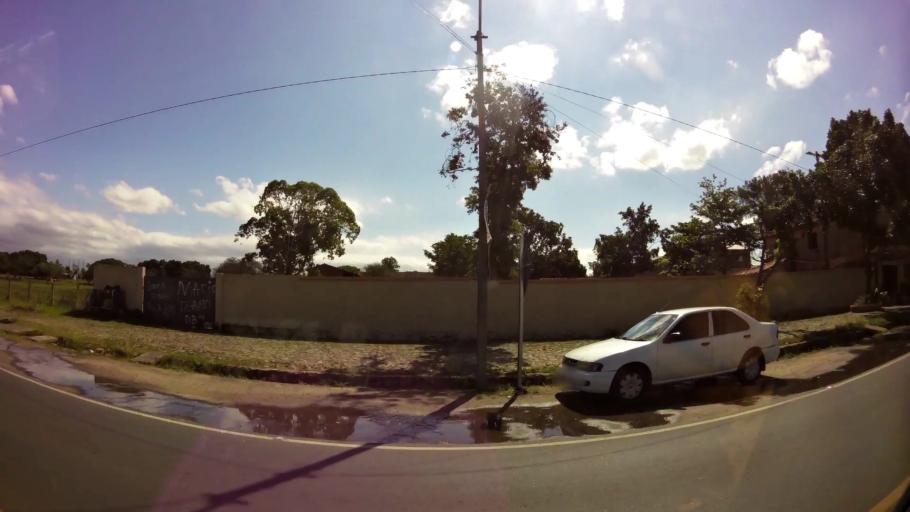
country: PY
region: Central
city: Fernando de la Mora
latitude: -25.2714
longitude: -57.5227
